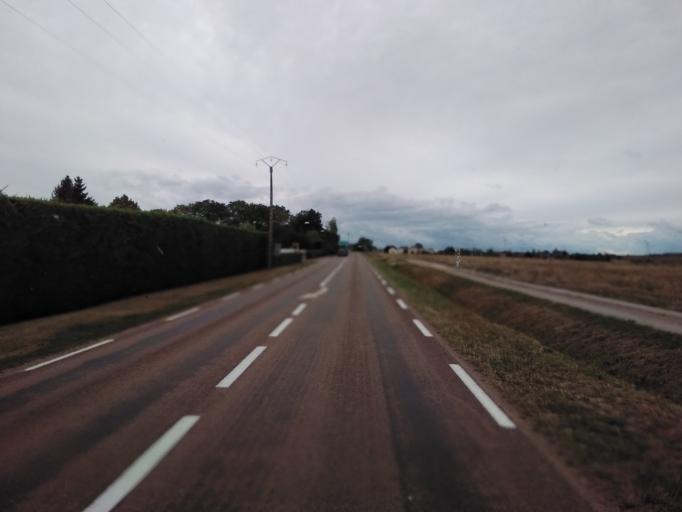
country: FR
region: Champagne-Ardenne
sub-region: Departement de l'Aube
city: Vendeuvre-sur-Barse
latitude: 48.1777
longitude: 4.4334
